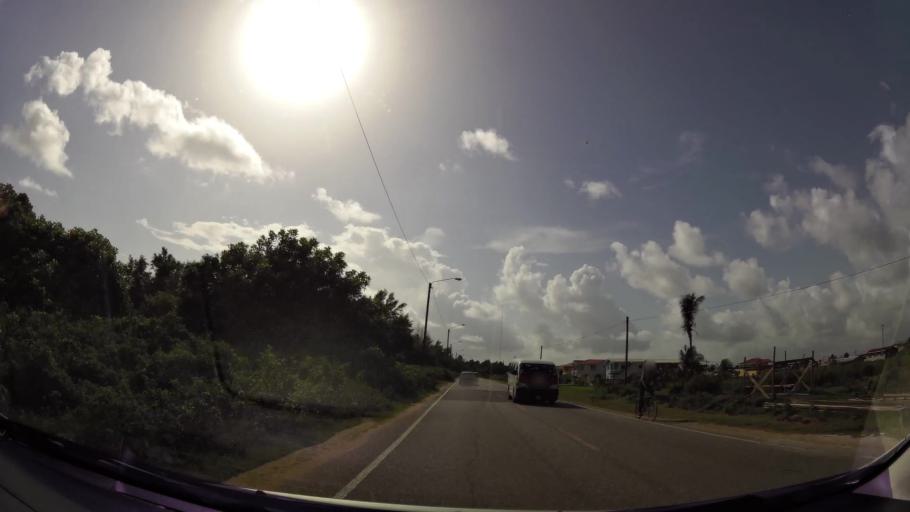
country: GY
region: Demerara-Mahaica
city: Mahaica Village
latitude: 6.7373
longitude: -57.9501
